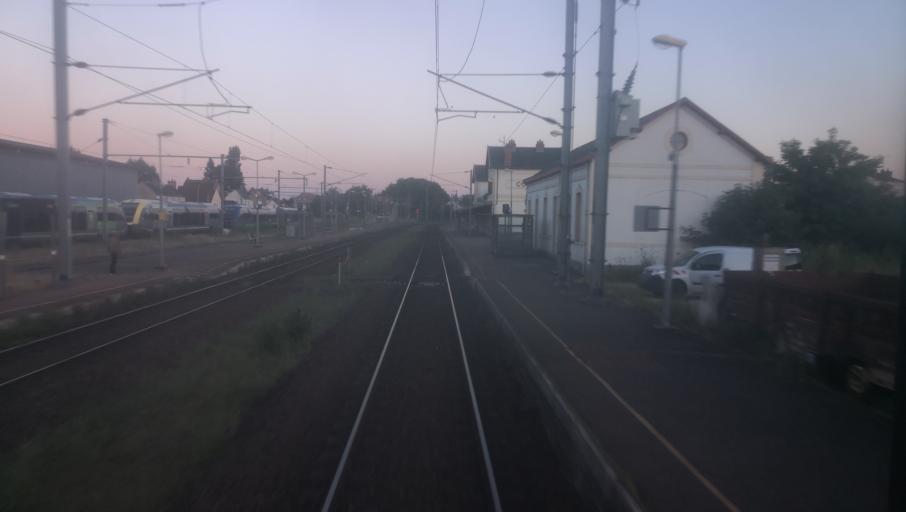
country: FR
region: Bourgogne
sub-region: Departement de la Nievre
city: Cosne-Cours-sur-Loire
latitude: 47.4148
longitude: 2.9318
